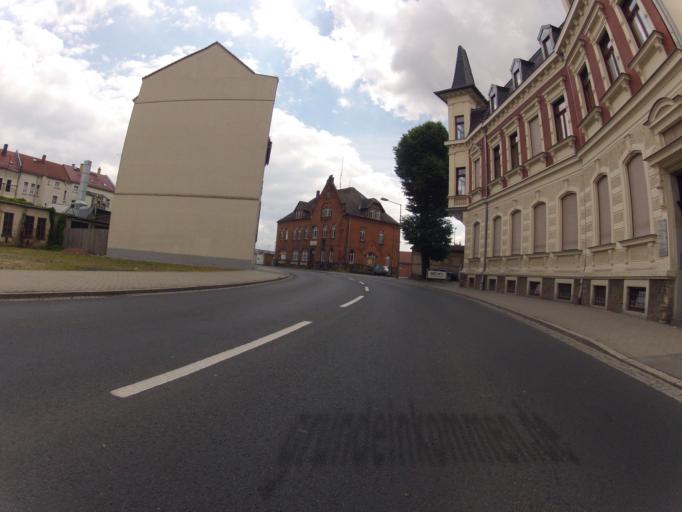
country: DE
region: Saxony
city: Wurzen
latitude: 51.3663
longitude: 12.7400
